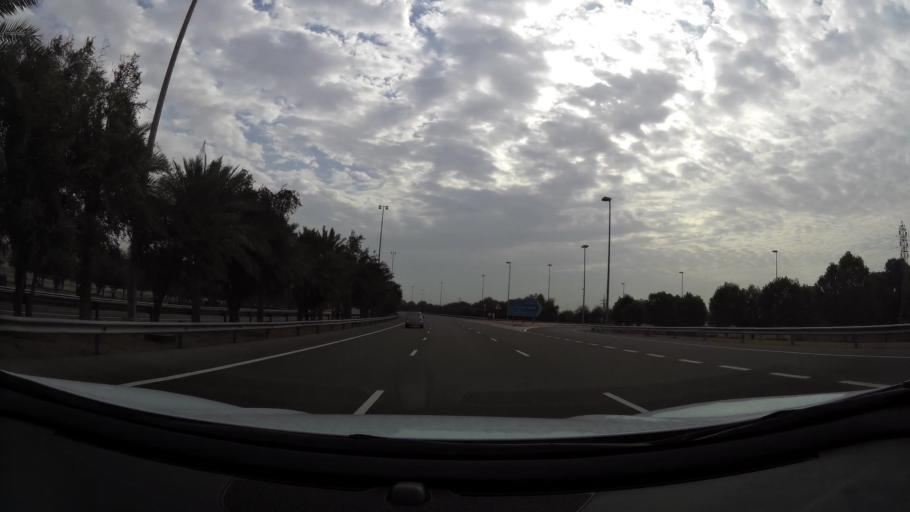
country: AE
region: Abu Dhabi
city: Al Ain
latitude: 24.2098
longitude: 55.5113
